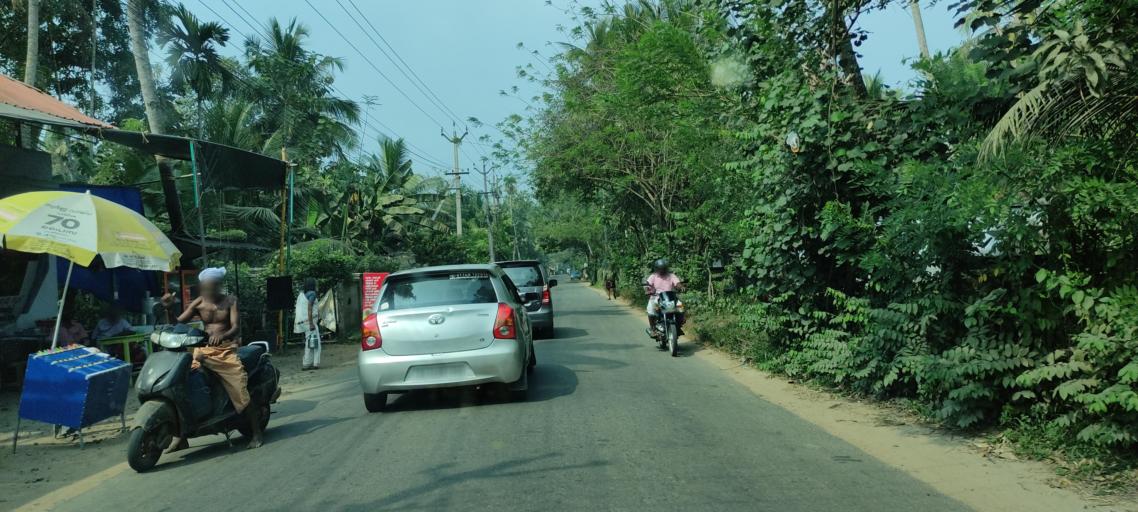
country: IN
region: Kerala
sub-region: Alappuzha
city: Shertallai
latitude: 9.6826
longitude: 76.4205
